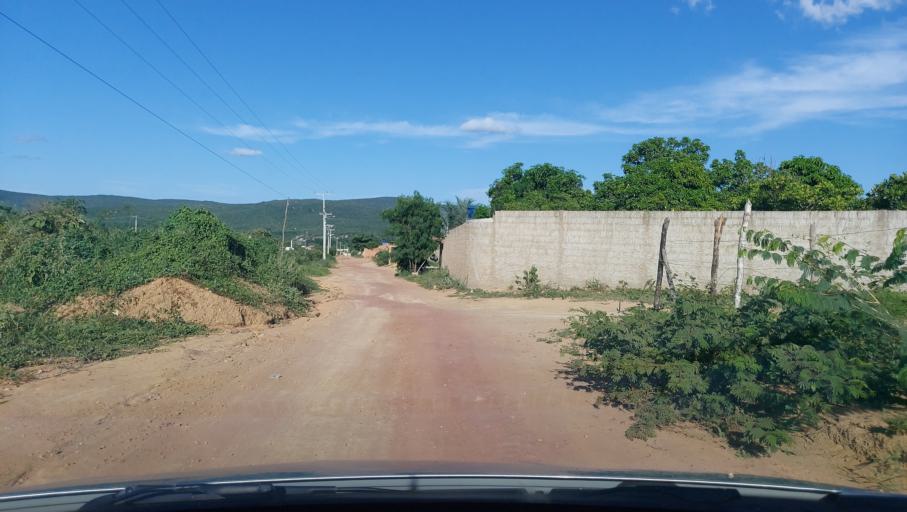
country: BR
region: Bahia
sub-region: Oliveira Dos Brejinhos
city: Beira Rio
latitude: -12.0054
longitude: -42.6341
